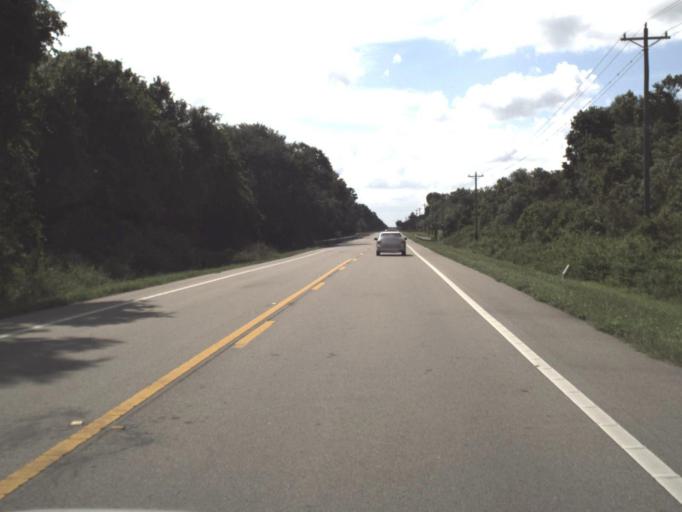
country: US
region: Florida
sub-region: Hillsborough County
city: Wimauma
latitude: 27.4598
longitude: -82.1449
